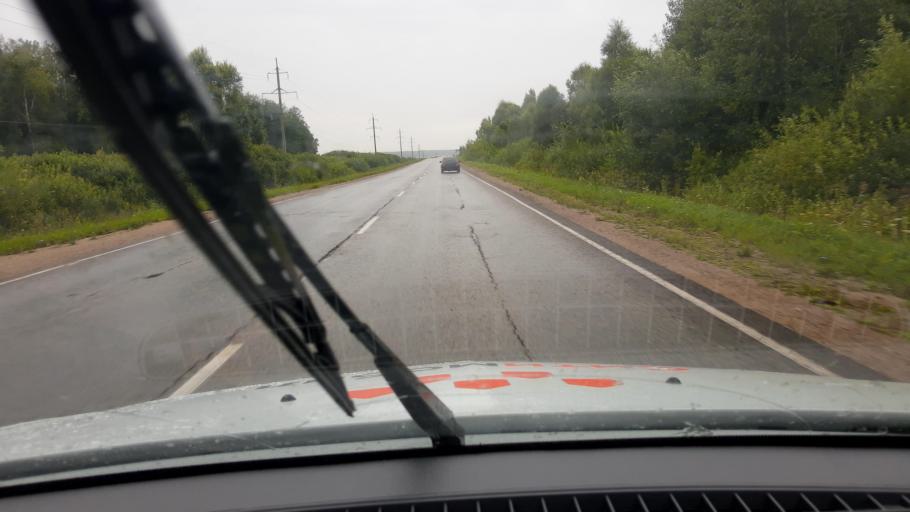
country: RU
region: Bashkortostan
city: Iglino
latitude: 54.8878
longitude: 56.4711
